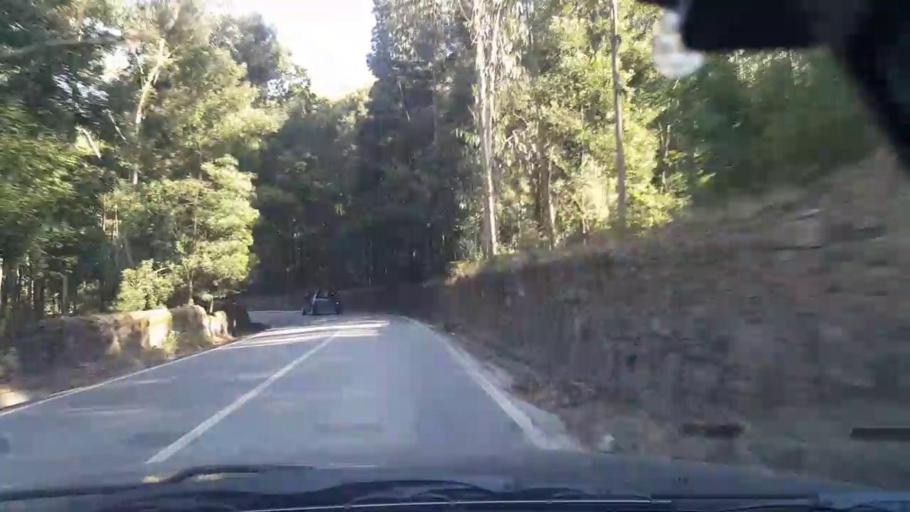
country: PT
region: Porto
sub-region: Maia
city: Gemunde
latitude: 41.3244
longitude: -8.6469
